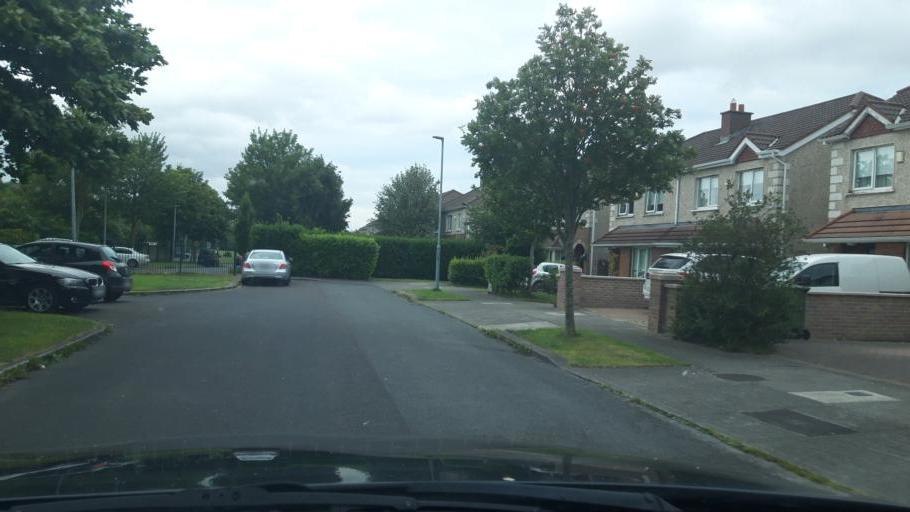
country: IE
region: Leinster
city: Hartstown
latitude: 53.4026
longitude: -6.4200
